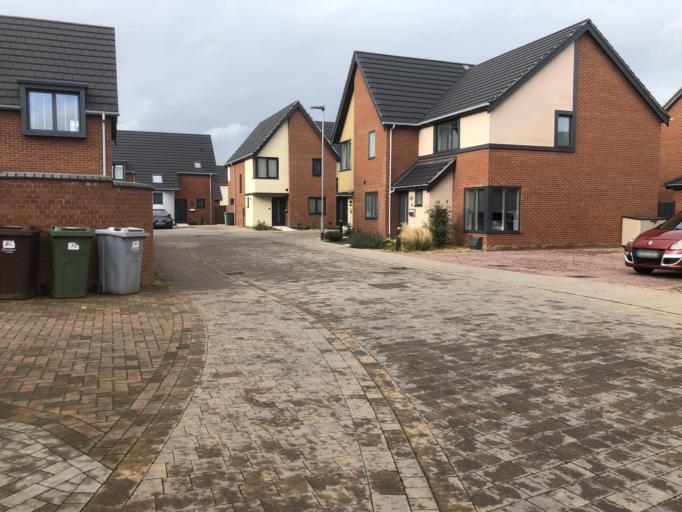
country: GB
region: England
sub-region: Norfolk
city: Spixworth
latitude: 52.6609
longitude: 1.3367
